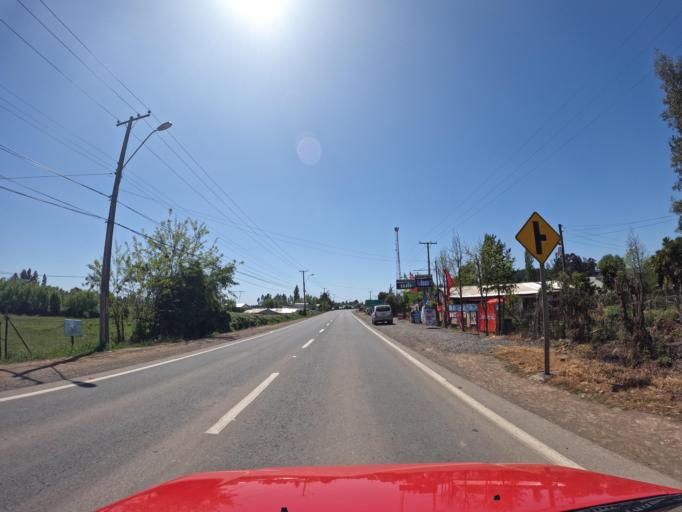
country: CL
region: Maule
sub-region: Provincia de Linares
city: Colbun
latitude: -35.7347
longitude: -71.4212
